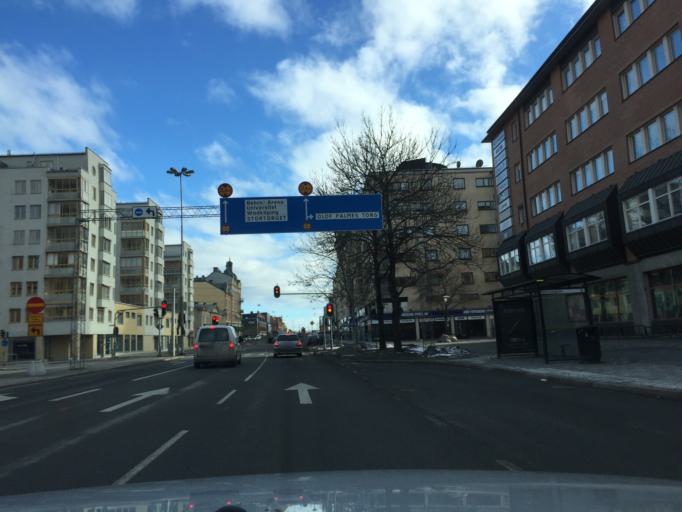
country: SE
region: OErebro
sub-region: Orebro Kommun
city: Orebro
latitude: 59.2703
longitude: 15.2061
